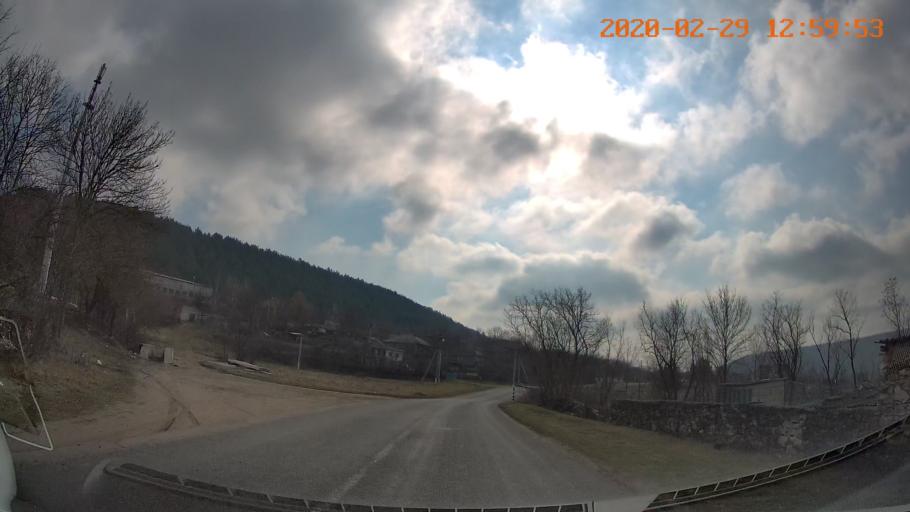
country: MD
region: Telenesti
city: Camenca
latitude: 48.0576
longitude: 28.7248
